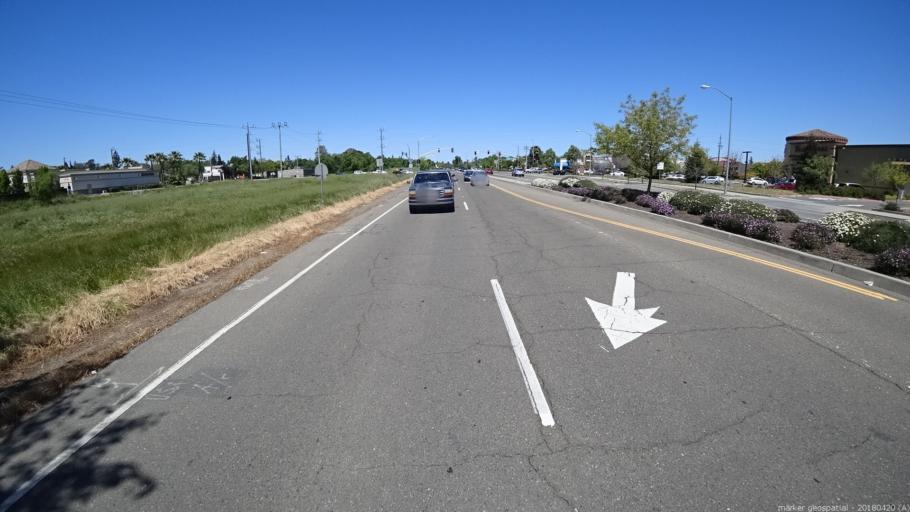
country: US
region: California
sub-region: Sacramento County
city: Parkway
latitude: 38.4803
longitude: -121.5051
